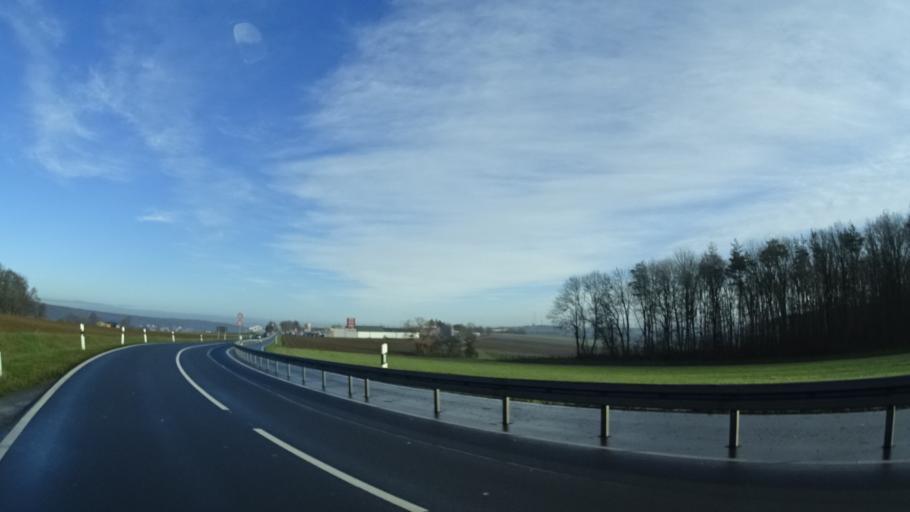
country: DE
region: Bavaria
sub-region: Regierungsbezirk Unterfranken
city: Wuerzburg
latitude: 49.7655
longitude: 9.8590
